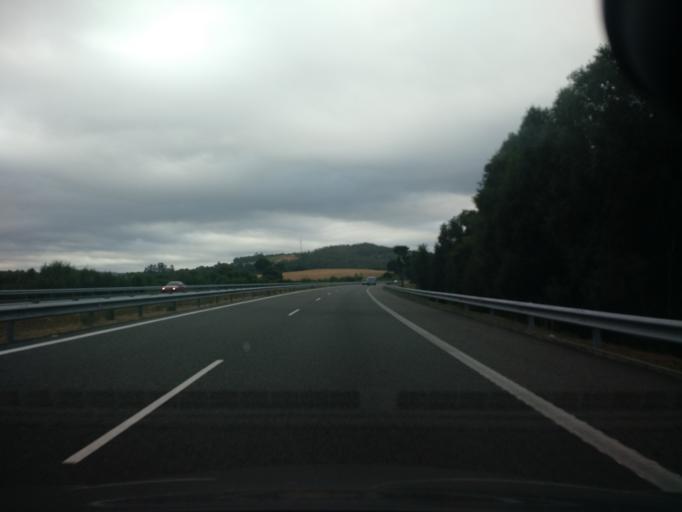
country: ES
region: Galicia
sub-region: Provincia da Coruna
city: Abegondo
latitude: 43.2421
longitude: -8.2566
